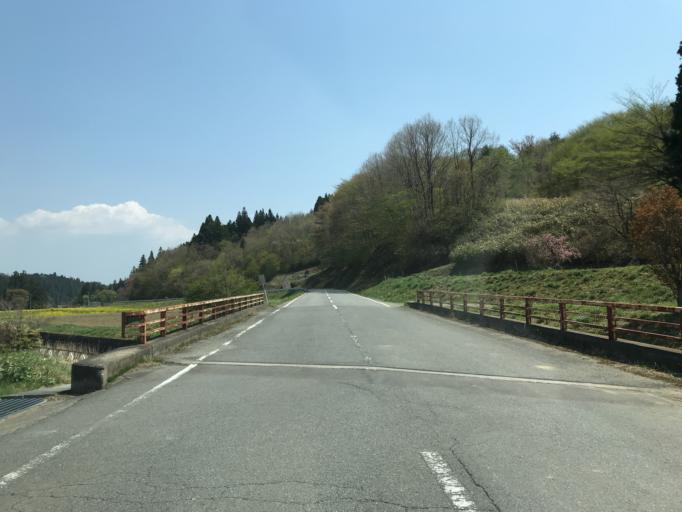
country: JP
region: Ibaraki
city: Kitaibaraki
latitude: 36.9697
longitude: 140.6494
